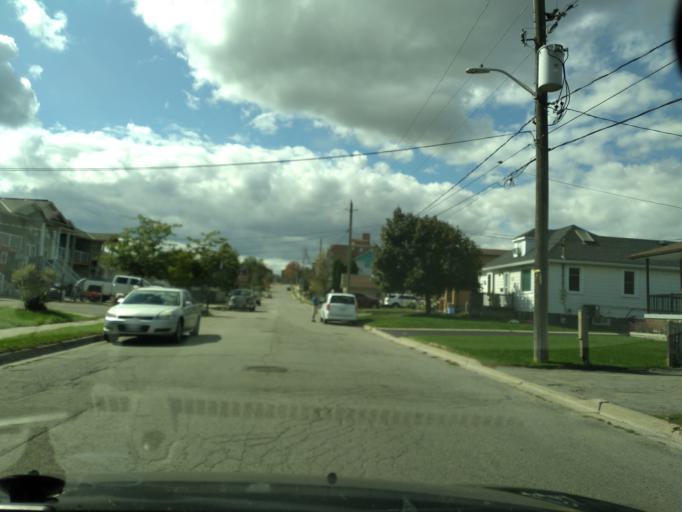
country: CA
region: Ontario
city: Bradford West Gwillimbury
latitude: 44.1142
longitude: -79.5603
